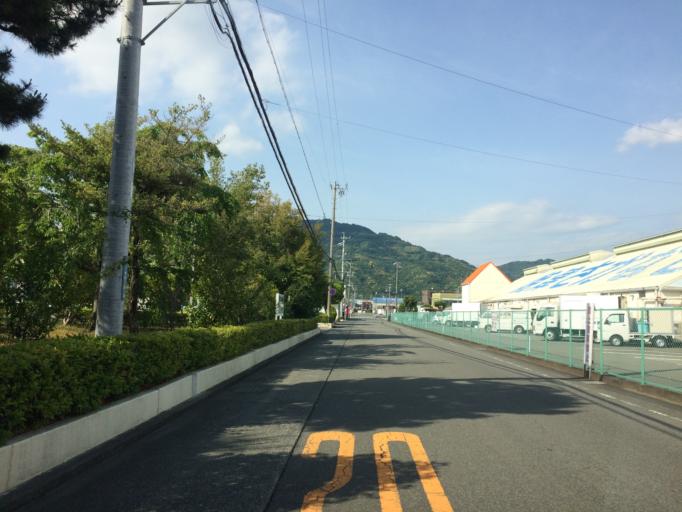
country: JP
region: Shizuoka
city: Yaizu
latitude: 34.8800
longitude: 138.3023
